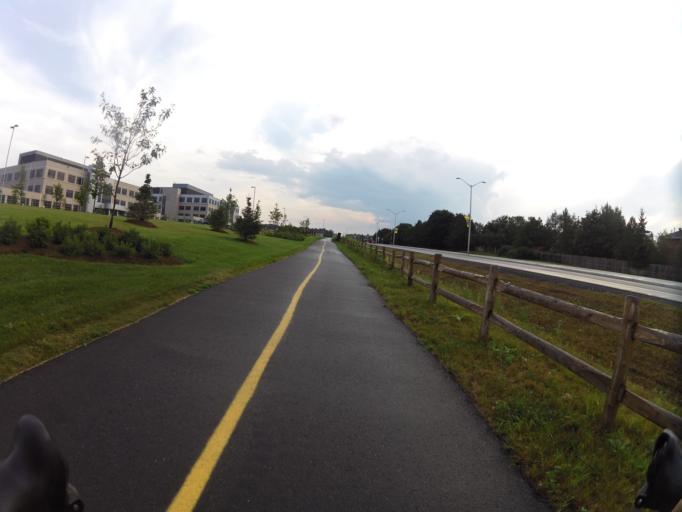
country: CA
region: Ontario
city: Bells Corners
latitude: 45.3472
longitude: -75.9273
